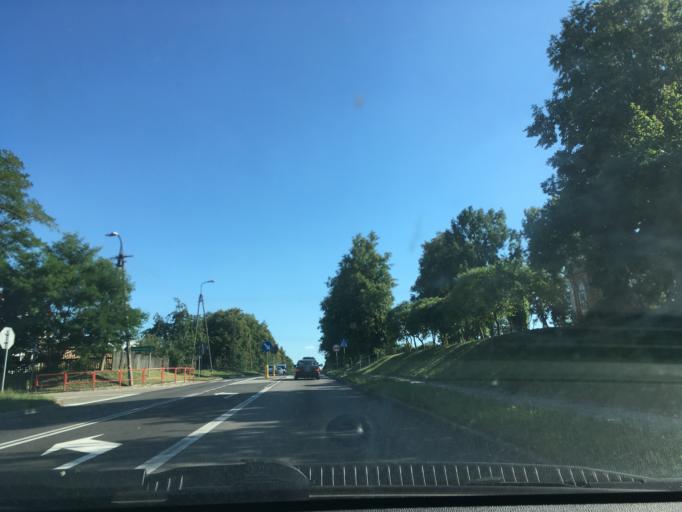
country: PL
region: Podlasie
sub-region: Powiat sokolski
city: Suchowola
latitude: 53.5348
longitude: 23.1052
